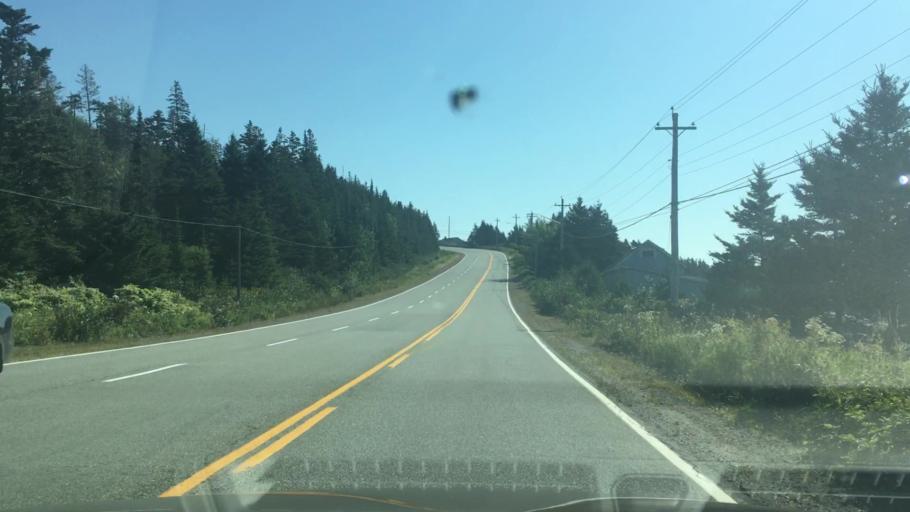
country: CA
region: Nova Scotia
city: New Glasgow
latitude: 44.8144
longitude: -62.6369
